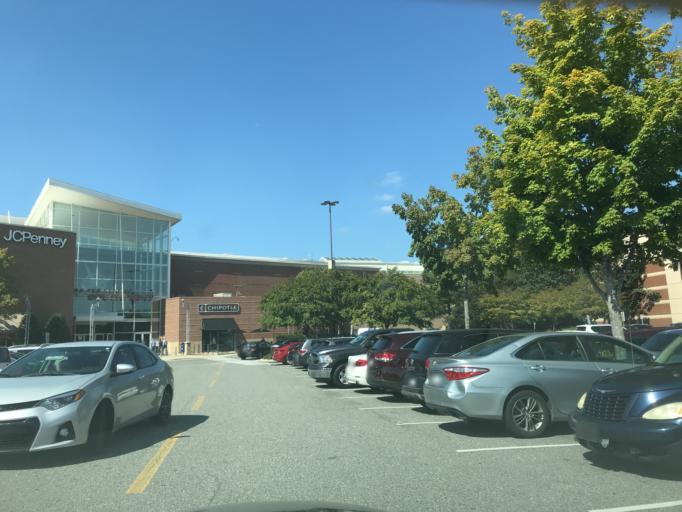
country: US
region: North Carolina
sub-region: Durham County
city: Durham
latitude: 35.9032
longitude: -78.9408
